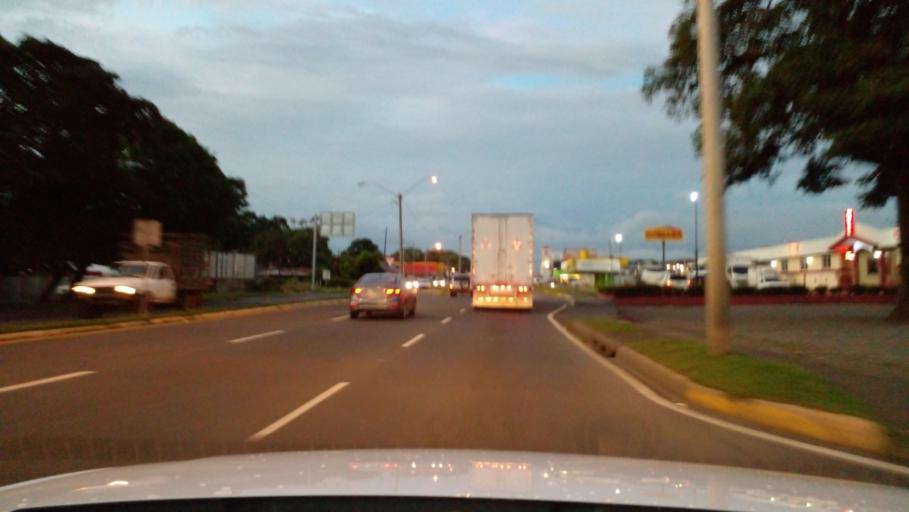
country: PA
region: Chiriqui
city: David
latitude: 8.4318
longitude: -82.4420
